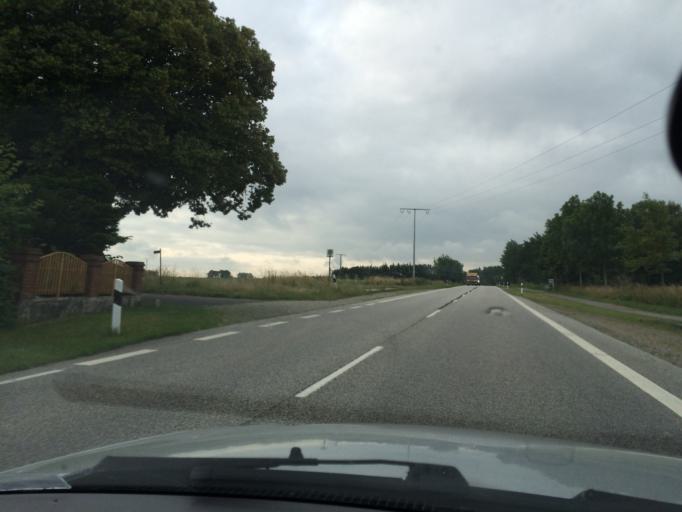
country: DE
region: Schleswig-Holstein
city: Oeversee
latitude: 54.6737
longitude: 9.4399
